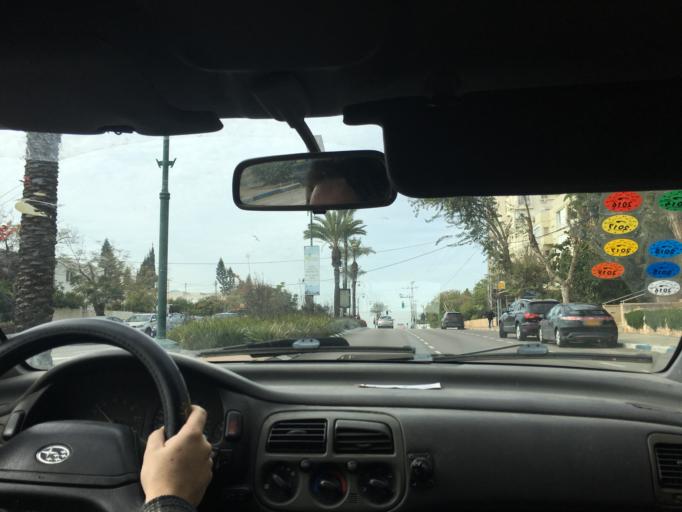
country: IL
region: Tel Aviv
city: Ramat HaSharon
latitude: 32.1373
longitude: 34.8400
